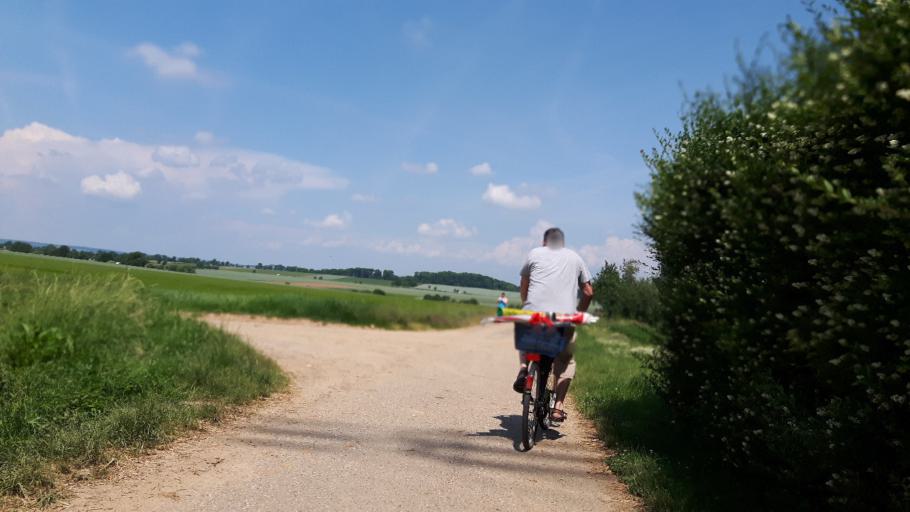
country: DE
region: Baden-Wuerttemberg
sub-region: Regierungsbezirk Stuttgart
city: Oedheim
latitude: 49.2209
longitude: 9.2514
